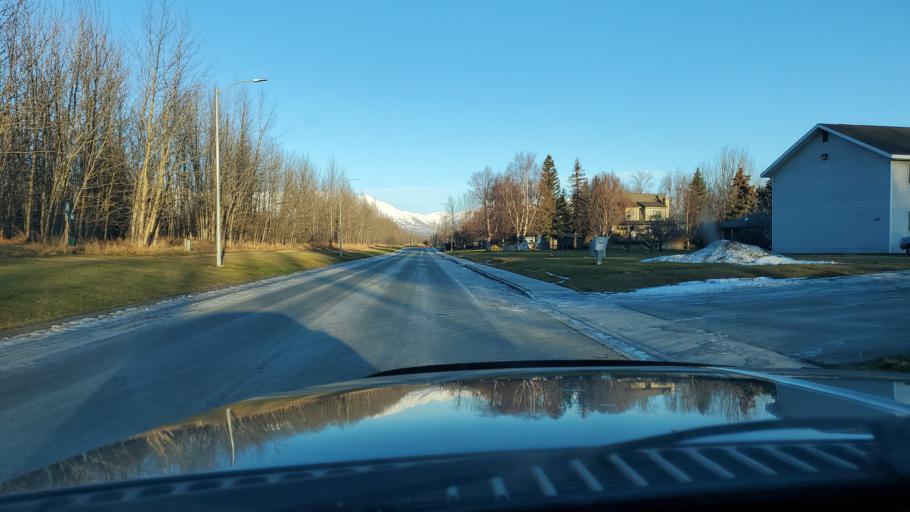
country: US
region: Alaska
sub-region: Matanuska-Susitna Borough
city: Palmer
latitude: 61.6087
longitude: -149.1092
